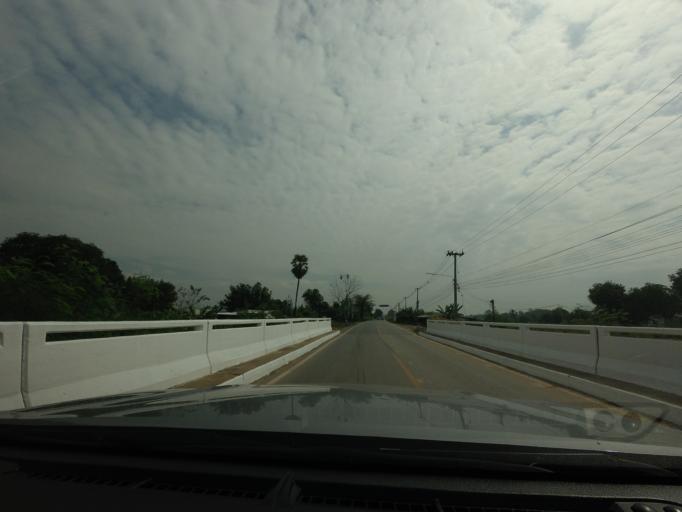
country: TH
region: Phitsanulok
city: Phitsanulok
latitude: 16.7331
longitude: 100.2969
